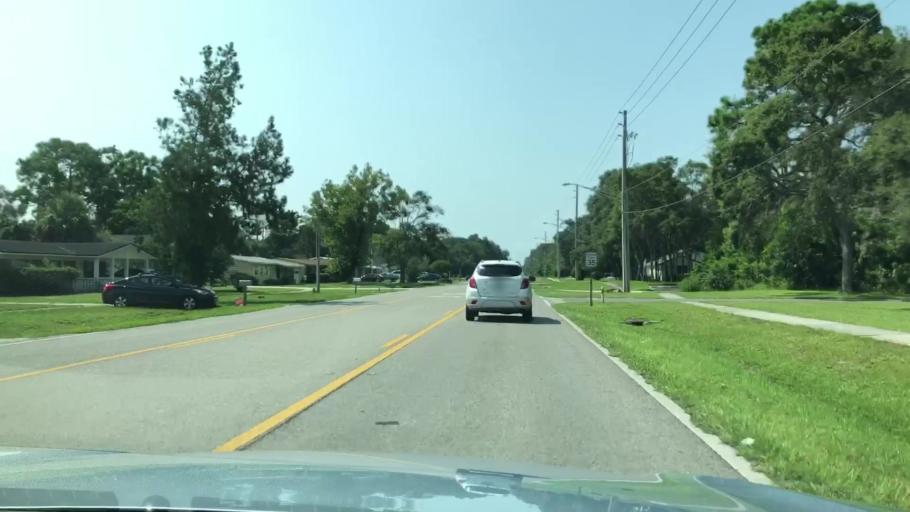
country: US
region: Florida
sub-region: Duval County
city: Atlantic Beach
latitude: 30.3221
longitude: -81.4088
